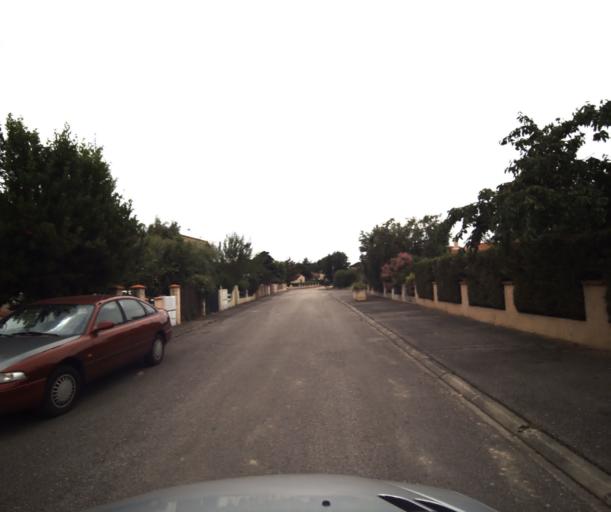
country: FR
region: Midi-Pyrenees
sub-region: Departement de la Haute-Garonne
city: Labarthe-sur-Leze
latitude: 43.4510
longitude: 1.4049
